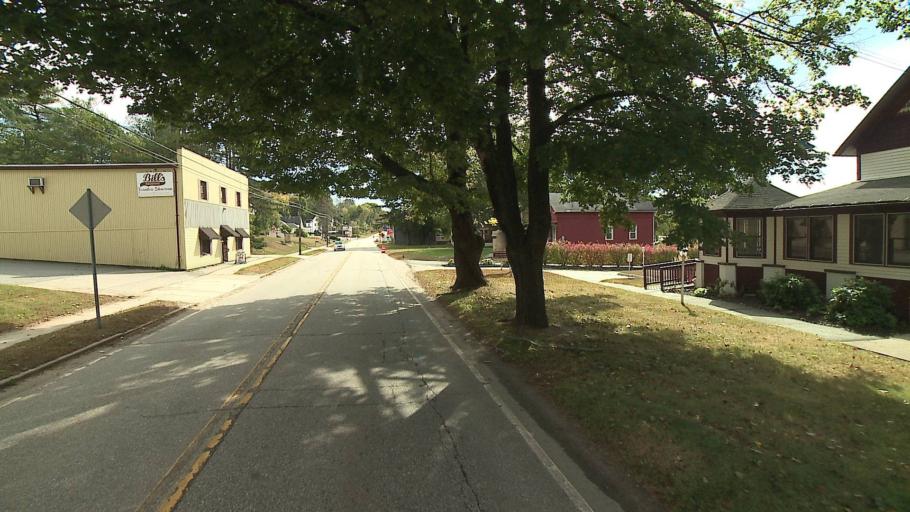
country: US
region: Connecticut
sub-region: Windham County
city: Danielson
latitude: 41.8176
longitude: -71.8774
